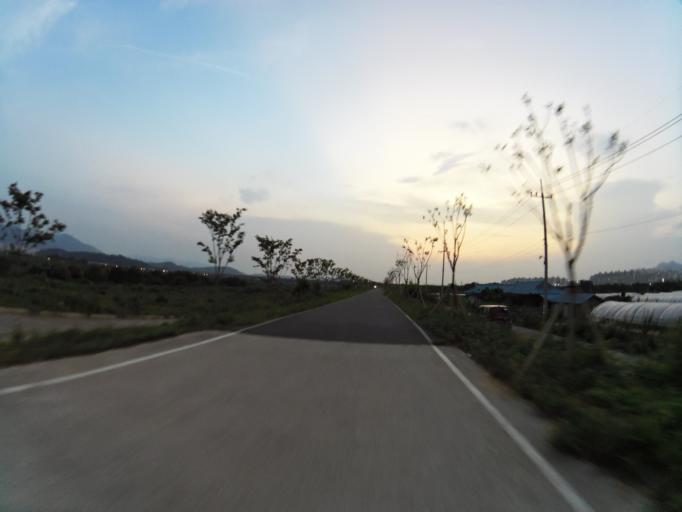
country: KR
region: Gyeongsangbuk-do
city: Gyeongsan-si
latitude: 35.8582
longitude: 128.7329
